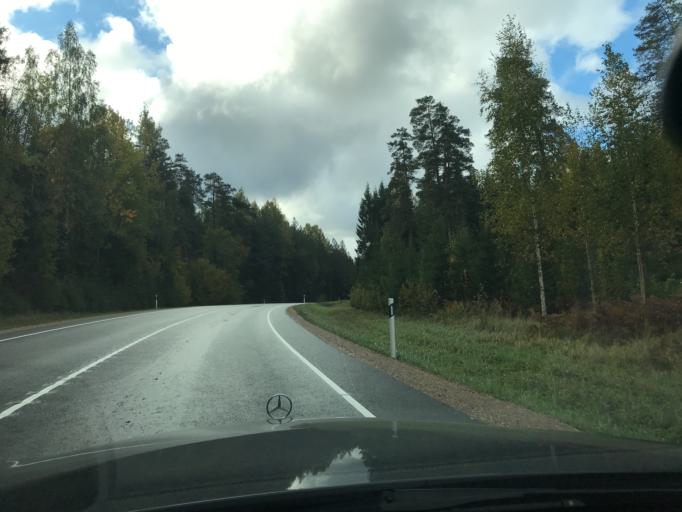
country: EE
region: Viljandimaa
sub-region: Karksi vald
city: Karksi-Nuia
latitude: 58.0436
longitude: 25.6465
